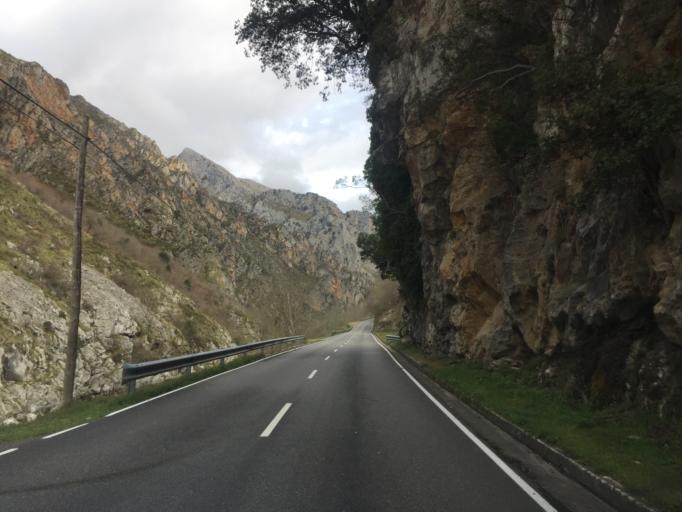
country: ES
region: Asturias
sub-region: Province of Asturias
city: Carrena
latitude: 43.2713
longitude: -4.8321
